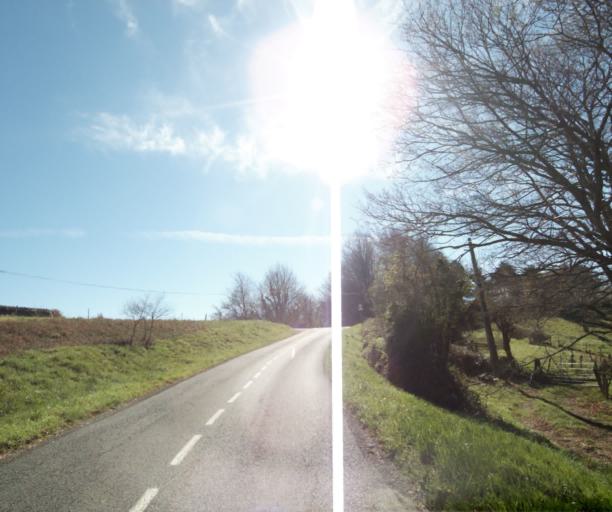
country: FR
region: Aquitaine
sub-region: Departement des Pyrenees-Atlantiques
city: Urrugne
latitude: 43.3570
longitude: -1.6756
